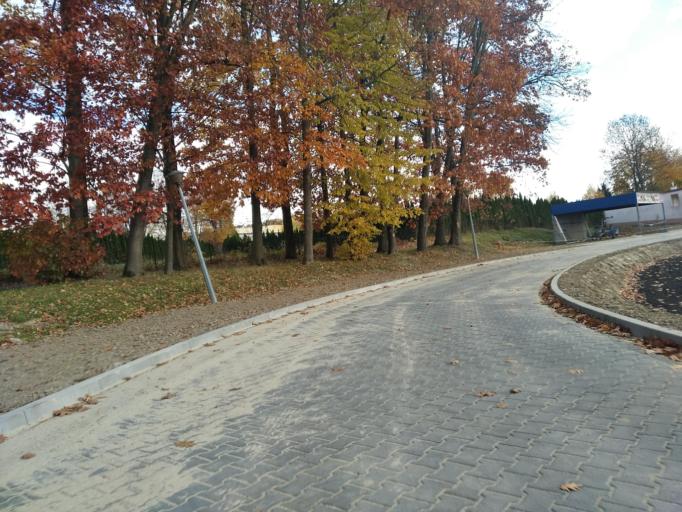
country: PL
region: Subcarpathian Voivodeship
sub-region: Powiat strzyzowski
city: Strzyzow
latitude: 49.8713
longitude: 21.7719
